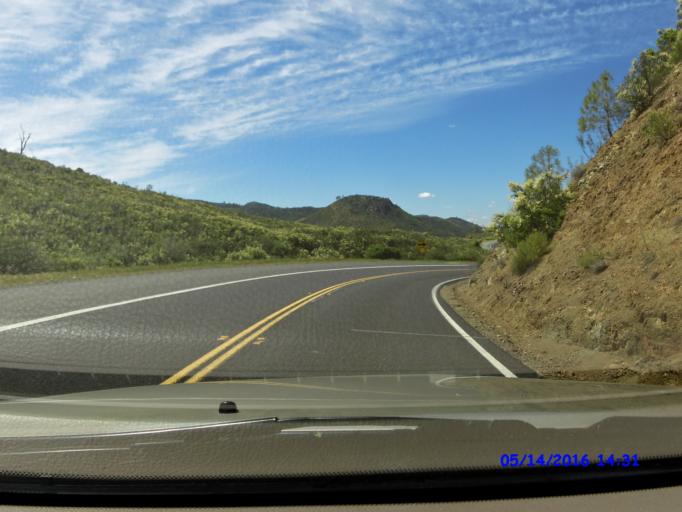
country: US
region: California
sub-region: Tuolumne County
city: Tuolumne City
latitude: 37.7586
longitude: -120.2516
